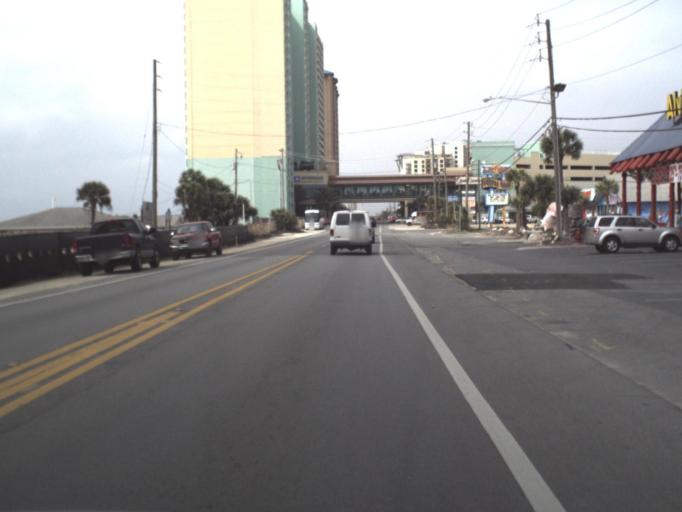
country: US
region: Florida
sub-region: Bay County
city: Panama City Beach
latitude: 30.2048
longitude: -85.8563
